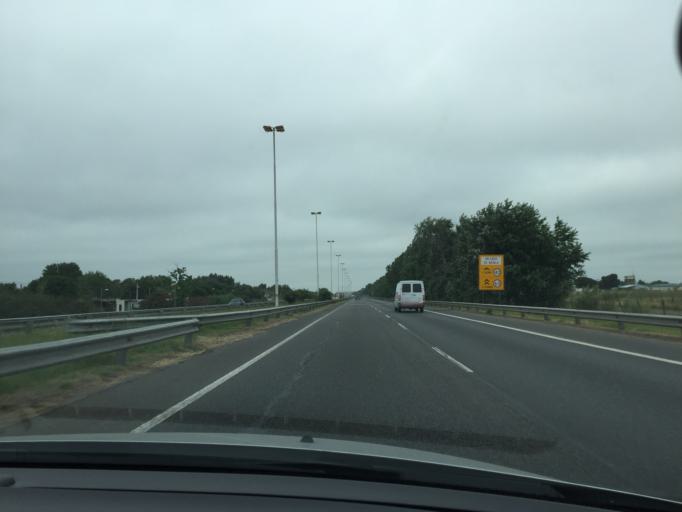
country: AR
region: Buenos Aires
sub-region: Partido de Ezeiza
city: Ezeiza
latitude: -34.8428
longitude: -58.5305
